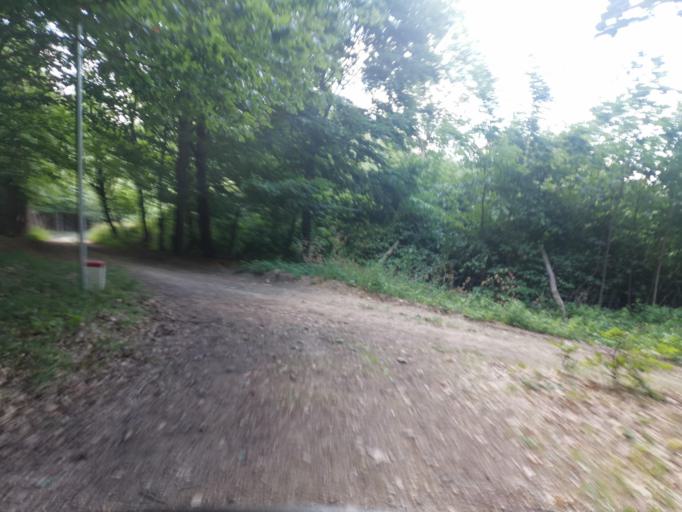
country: CZ
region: South Moravian
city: Knezdub
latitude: 48.8133
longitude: 17.3967
